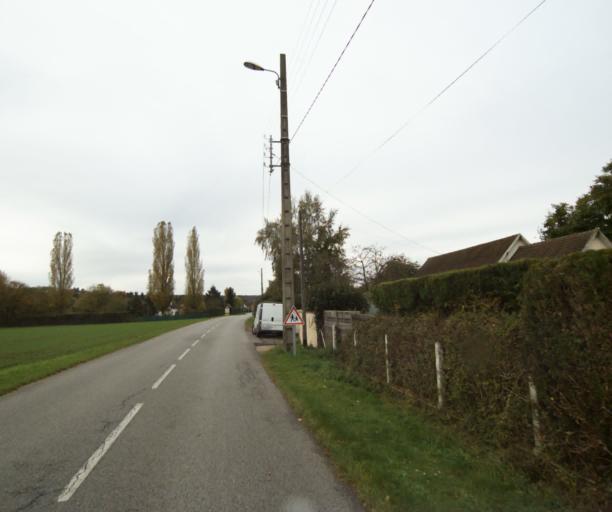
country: FR
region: Centre
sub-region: Departement d'Eure-et-Loir
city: Vert-en-Drouais
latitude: 48.7717
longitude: 1.3335
